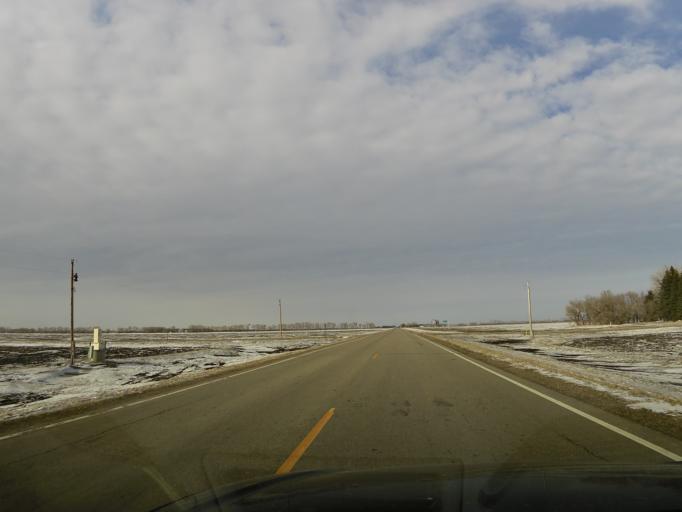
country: US
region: Minnesota
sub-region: Kittson County
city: Hallock
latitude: 48.5575
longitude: -97.1067
